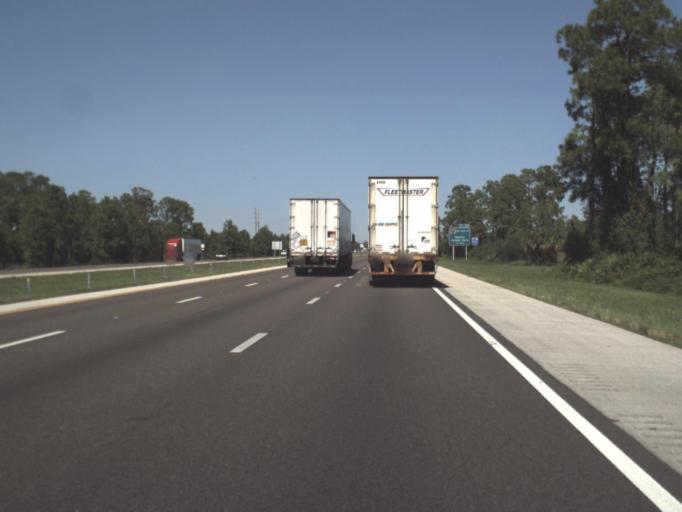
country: US
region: Florida
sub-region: Collier County
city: Vineyards
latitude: 26.1960
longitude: -81.7356
